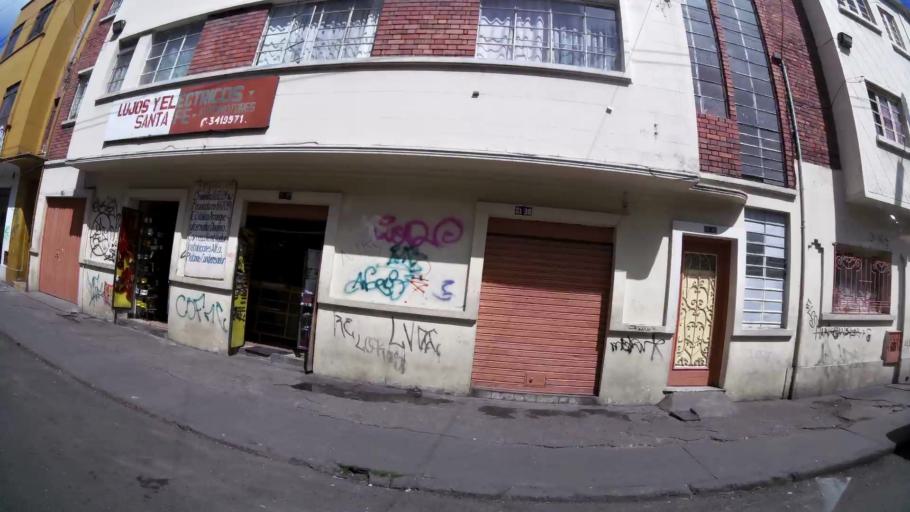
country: CO
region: Bogota D.C.
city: Bogota
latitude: 4.6113
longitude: -74.0764
